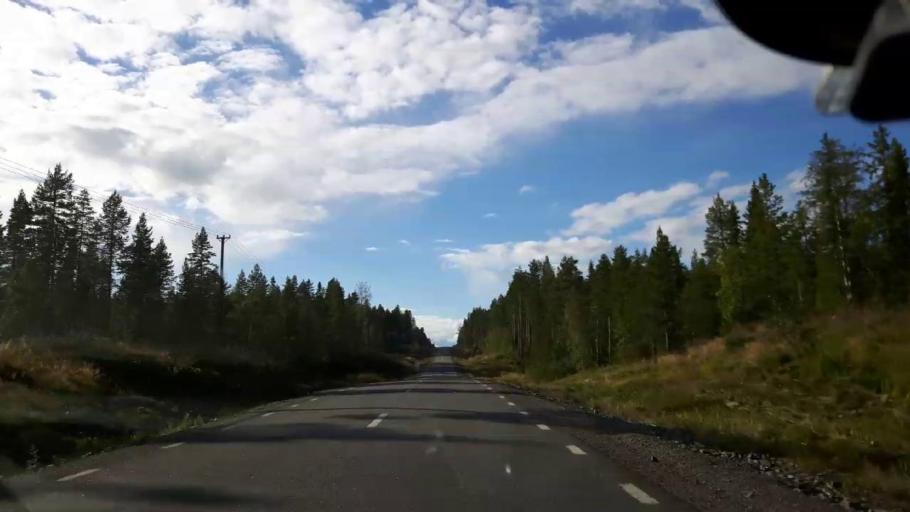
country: SE
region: Jaemtland
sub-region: Stroemsunds Kommun
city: Stroemsund
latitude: 63.5615
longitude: 15.8041
